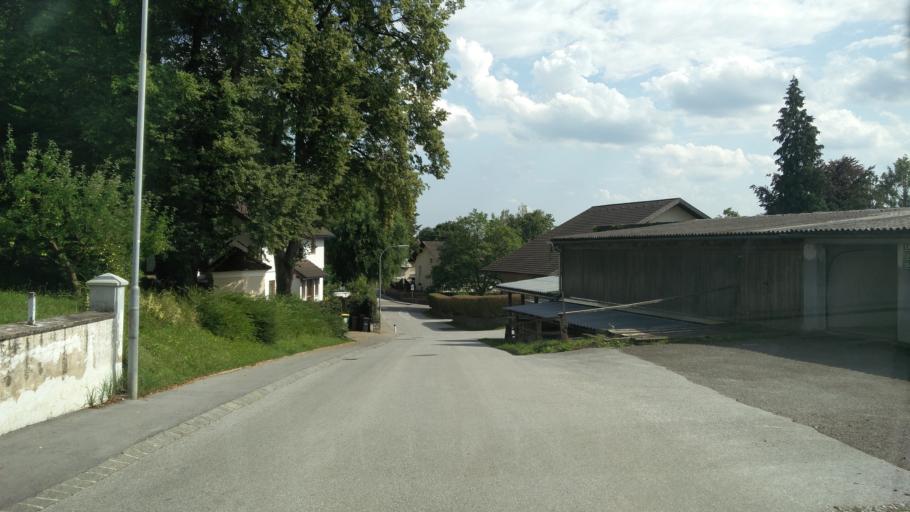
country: AT
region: Styria
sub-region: Politischer Bezirk Weiz
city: Weiz
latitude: 47.2226
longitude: 15.6312
